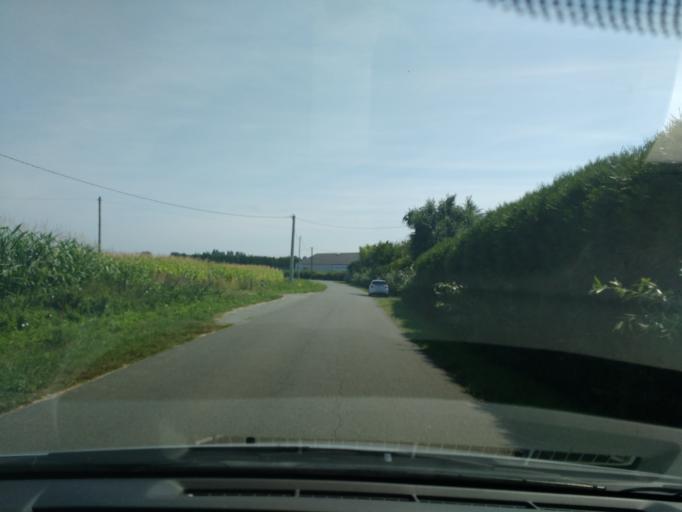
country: FR
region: Pays de la Loire
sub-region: Departement de Maine-et-Loire
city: Maze
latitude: 47.4732
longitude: -0.2579
